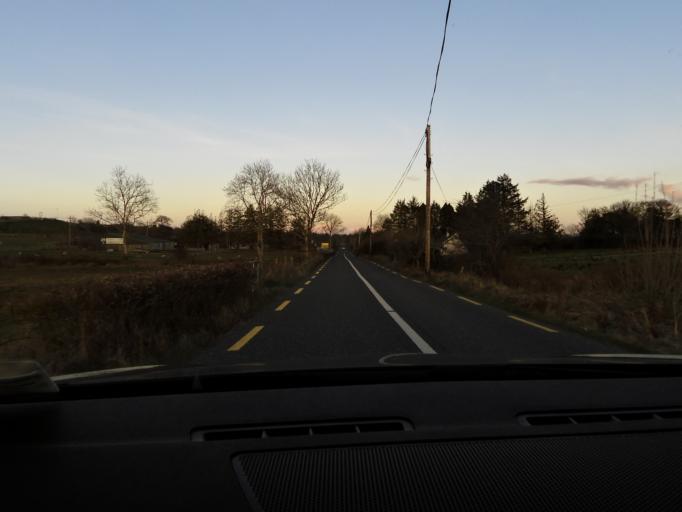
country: IE
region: Connaught
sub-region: Roscommon
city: Boyle
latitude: 53.9712
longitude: -8.4008
